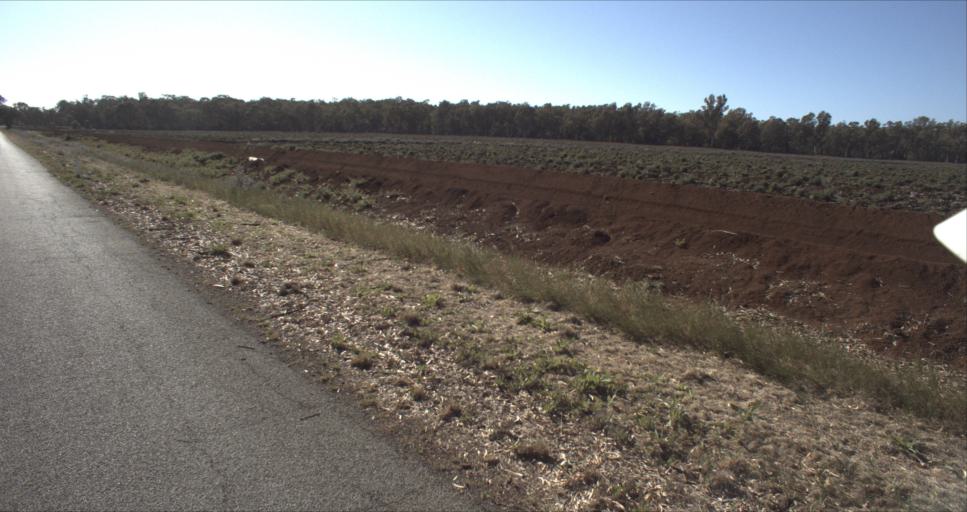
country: AU
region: New South Wales
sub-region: Leeton
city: Leeton
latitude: -34.6059
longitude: 146.2587
